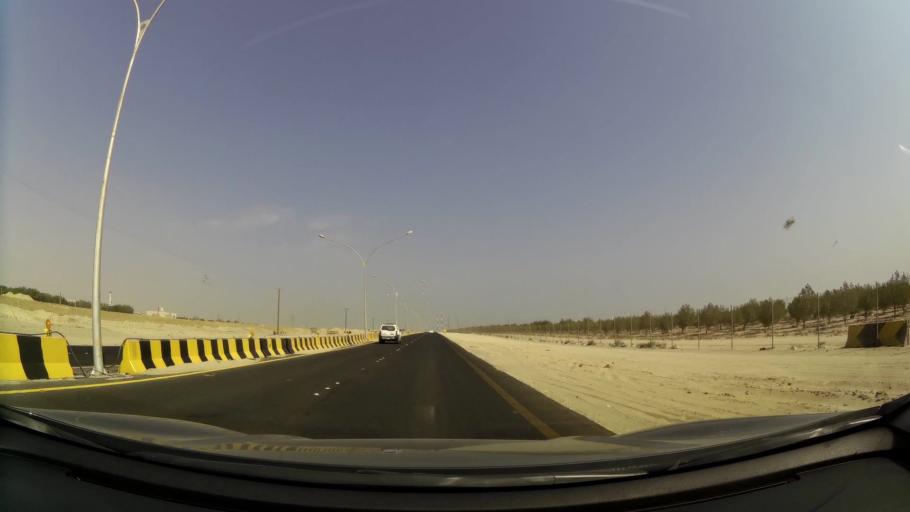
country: KW
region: Al Ahmadi
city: Al Fahahil
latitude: 28.9855
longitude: 48.1365
